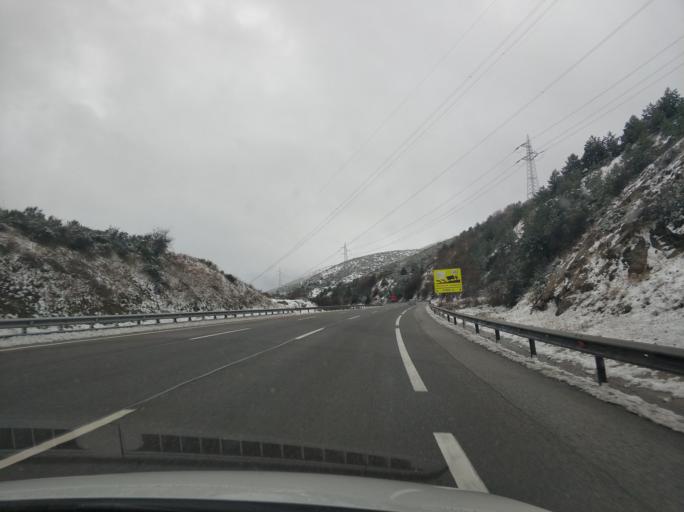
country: ES
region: Madrid
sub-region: Provincia de Madrid
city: Somosierra
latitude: 41.1587
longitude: -3.5850
